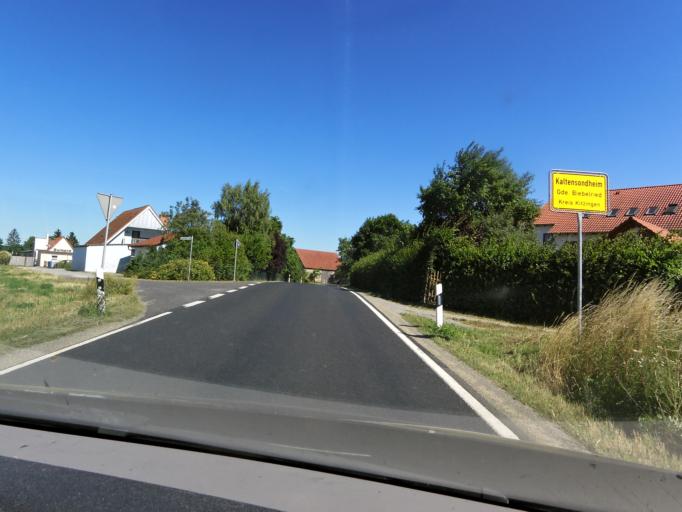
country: DE
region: Bavaria
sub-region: Regierungsbezirk Unterfranken
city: Biebelried
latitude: 49.7322
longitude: 10.0861
